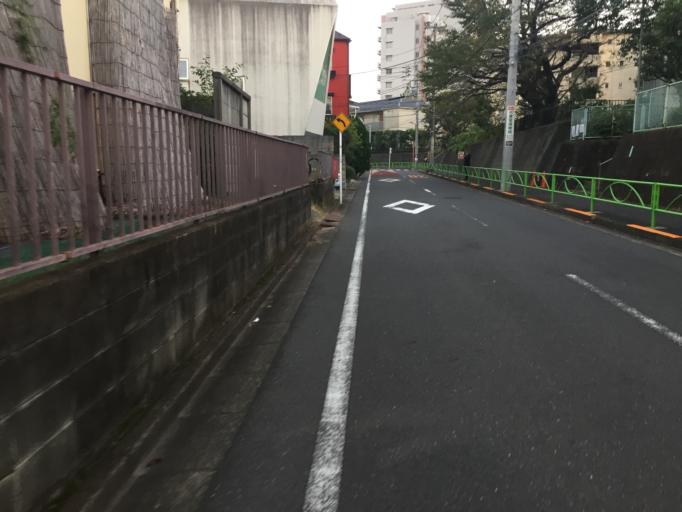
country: JP
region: Tokyo
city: Tokyo
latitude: 35.6292
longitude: 139.6661
